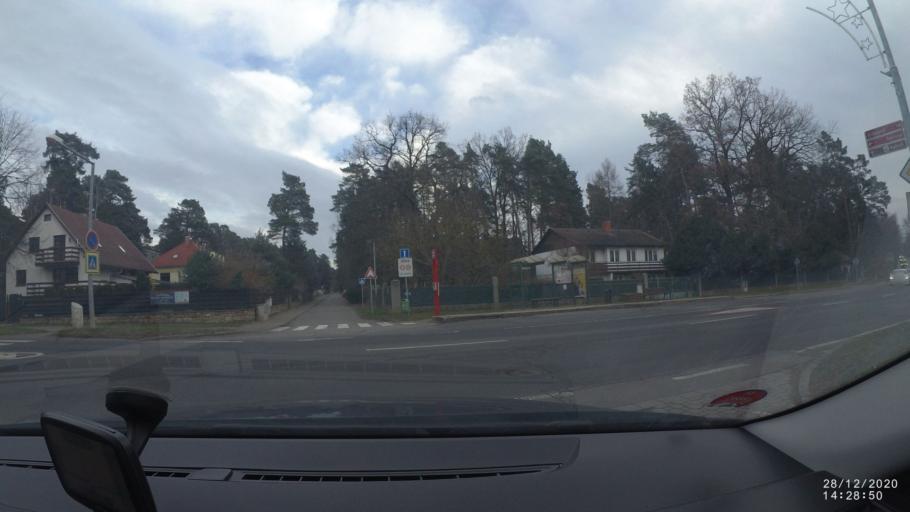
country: CZ
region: Central Bohemia
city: Sestajovice
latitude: 50.0900
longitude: 14.6663
